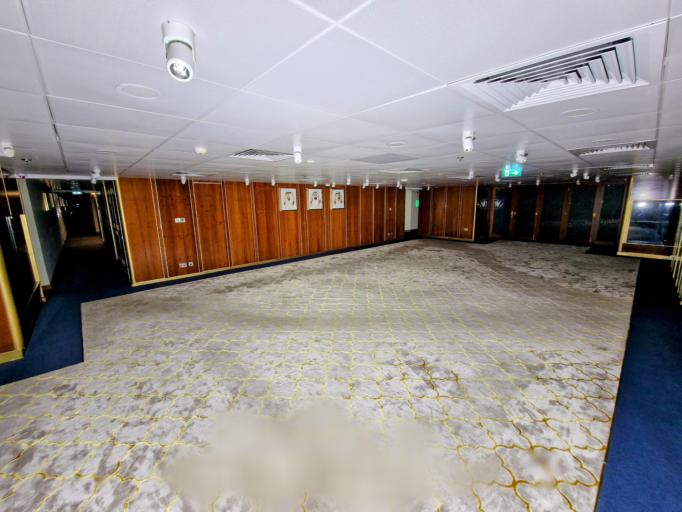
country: AE
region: Ash Shariqah
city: Sharjah
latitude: 25.2618
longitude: 55.2807
